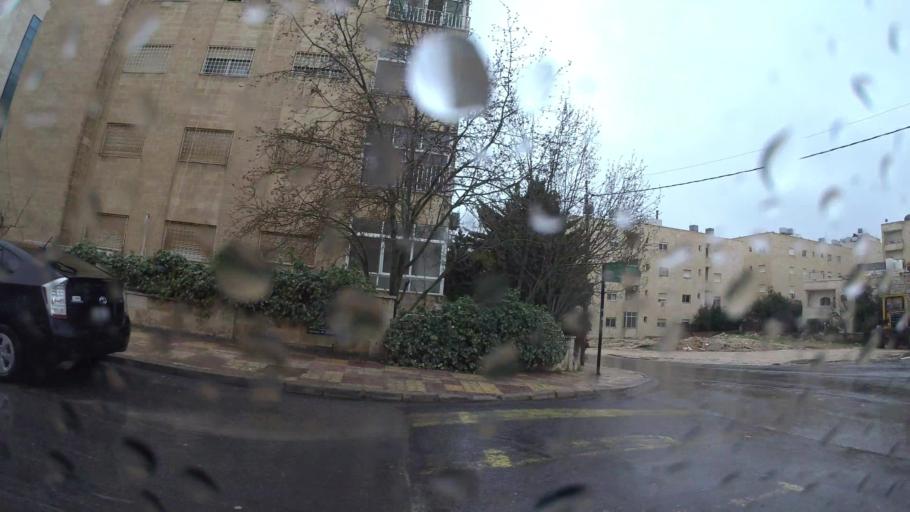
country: JO
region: Amman
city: Al Jubayhah
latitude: 32.0177
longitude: 35.8788
